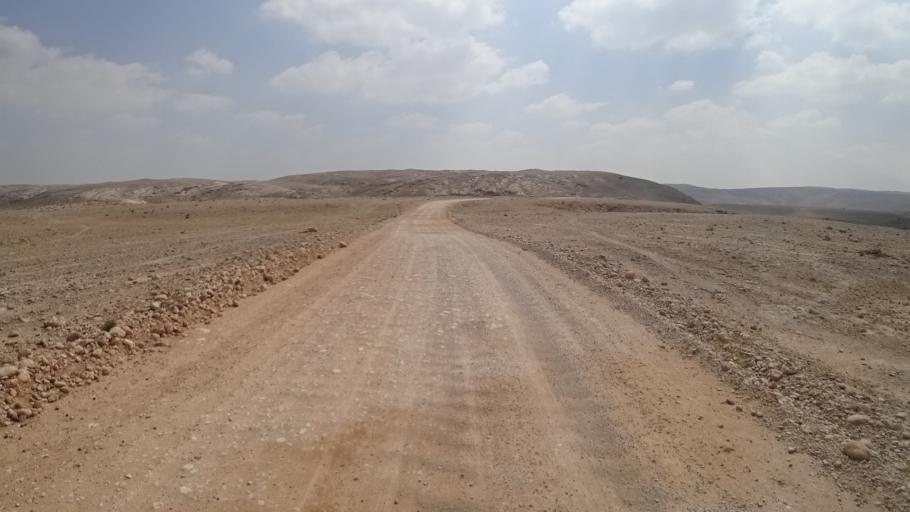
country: OM
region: Zufar
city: Salalah
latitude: 17.2387
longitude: 53.8954
